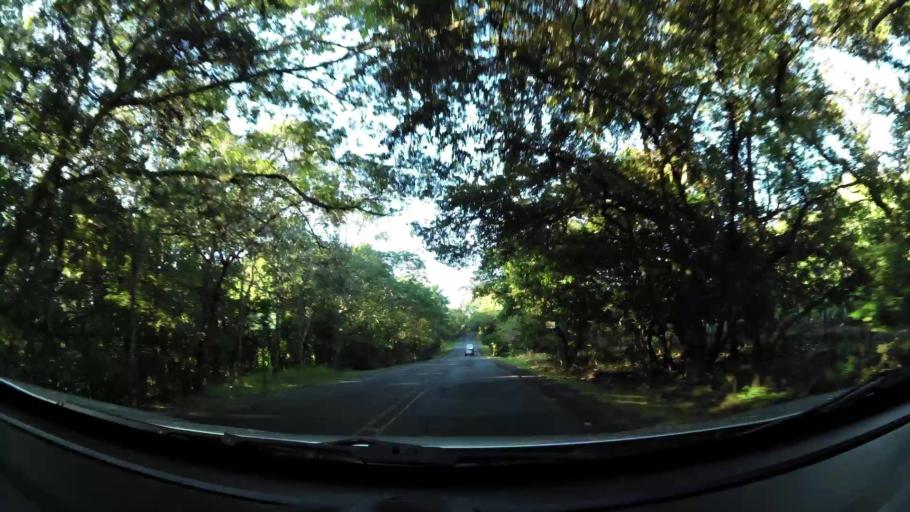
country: CR
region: Puntarenas
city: Miramar
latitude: 10.0984
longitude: -84.8124
